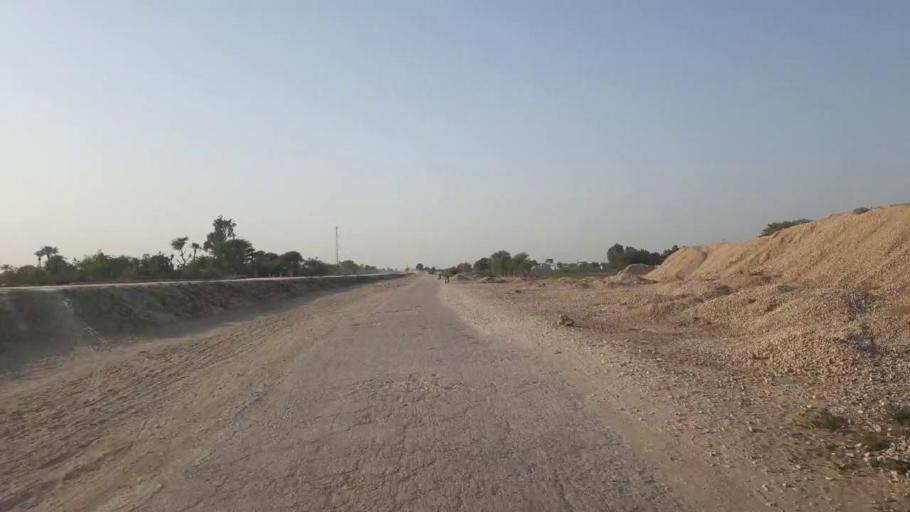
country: PK
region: Sindh
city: Dhoro Naro
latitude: 25.4928
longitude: 69.5650
